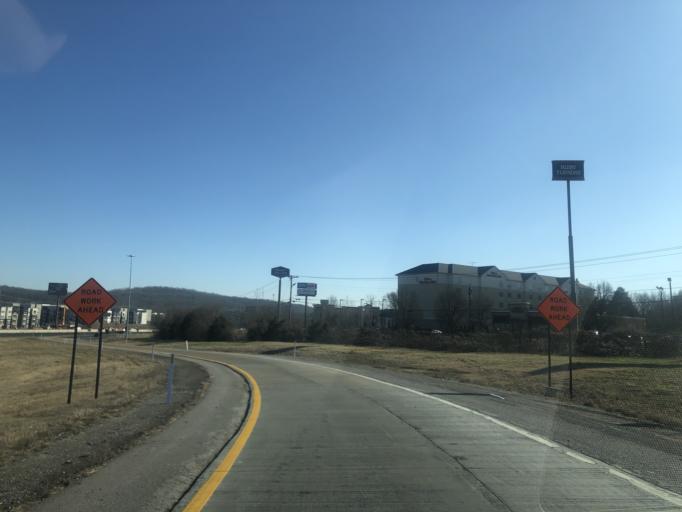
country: US
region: Tennessee
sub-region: Rutherford County
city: La Vergne
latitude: 35.9735
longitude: -86.5726
